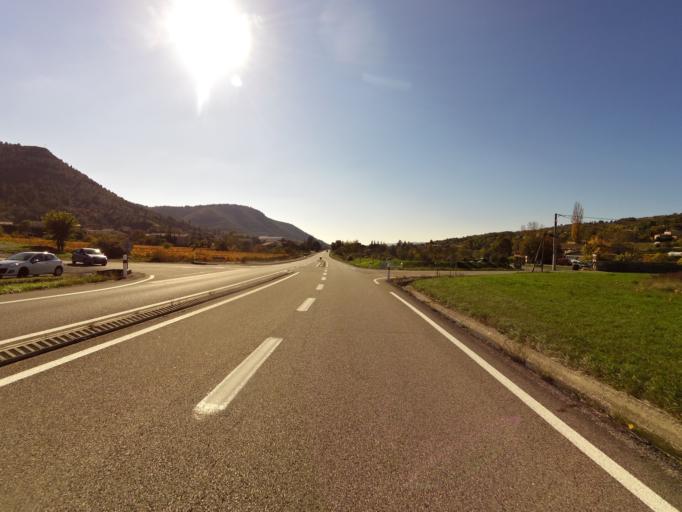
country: FR
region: Rhone-Alpes
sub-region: Departement de l'Ardeche
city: Vesseaux
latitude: 44.6571
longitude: 4.4481
